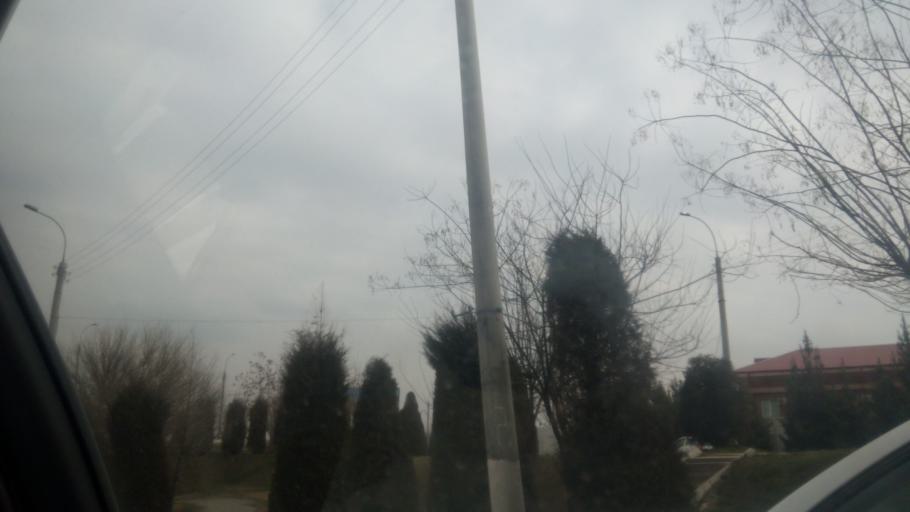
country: UZ
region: Toshkent
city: Salor
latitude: 41.3348
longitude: 69.3098
